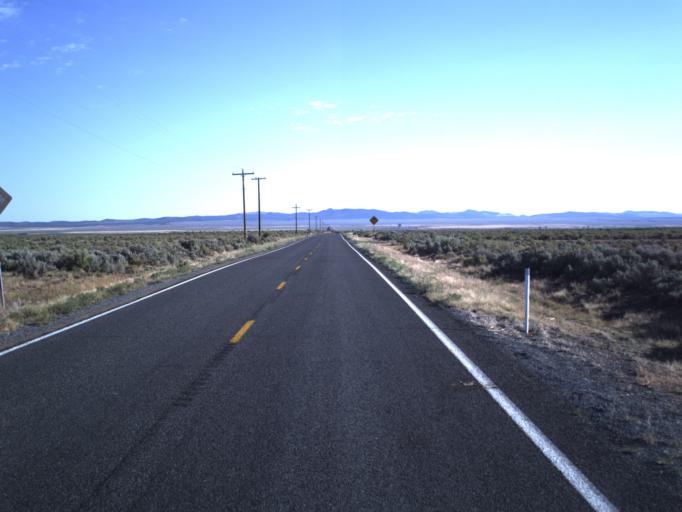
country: US
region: Utah
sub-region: Iron County
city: Enoch
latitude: 37.8304
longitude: -113.0503
